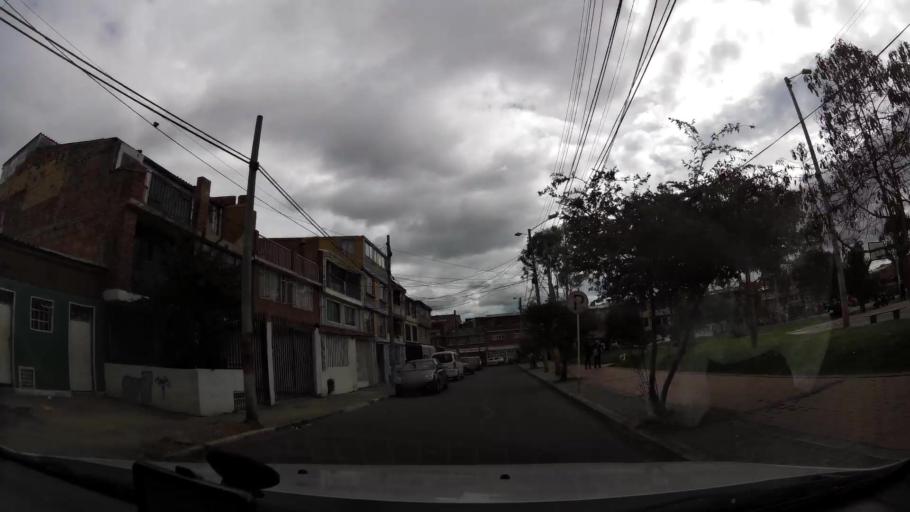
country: CO
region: Bogota D.C.
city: Bogota
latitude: 4.6020
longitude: -74.1302
